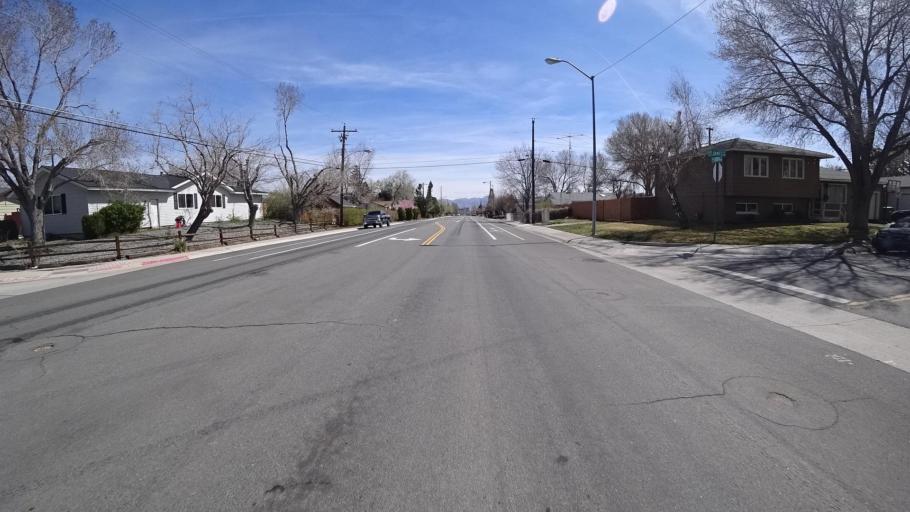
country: US
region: Nevada
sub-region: Washoe County
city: Reno
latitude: 39.5306
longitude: -119.8520
